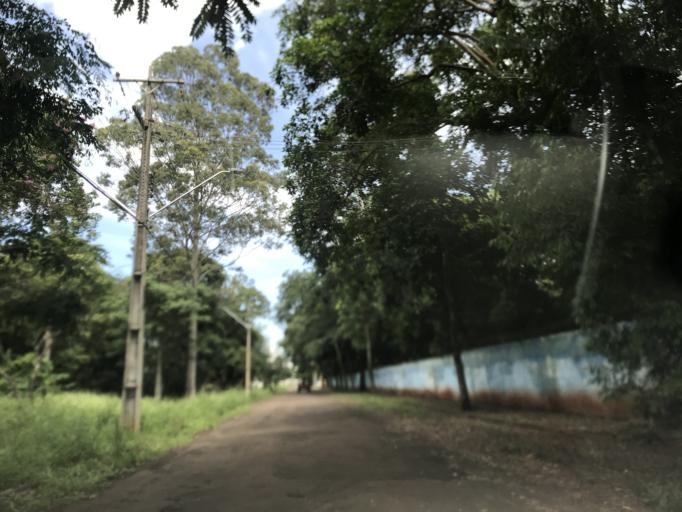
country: BR
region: Parana
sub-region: Londrina
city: Londrina
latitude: -23.3442
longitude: -51.1542
